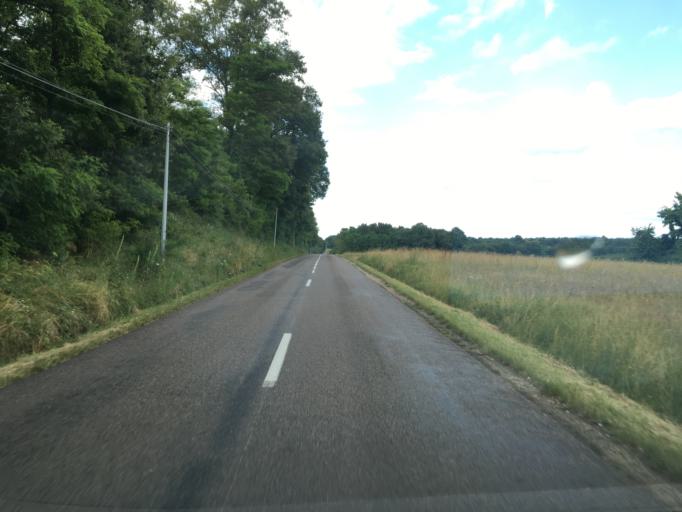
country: FR
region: Bourgogne
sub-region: Departement de l'Yonne
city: Charbuy
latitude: 47.8372
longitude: 3.4710
